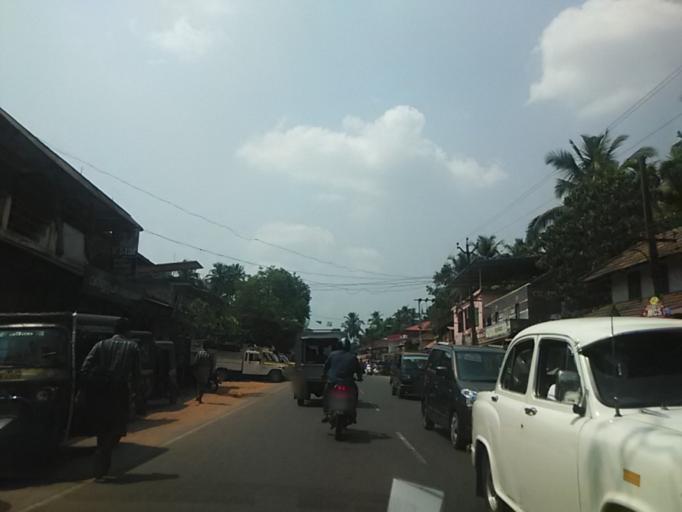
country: IN
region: Kerala
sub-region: Kozhikode
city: Naduvannur
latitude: 11.4857
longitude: 75.7752
